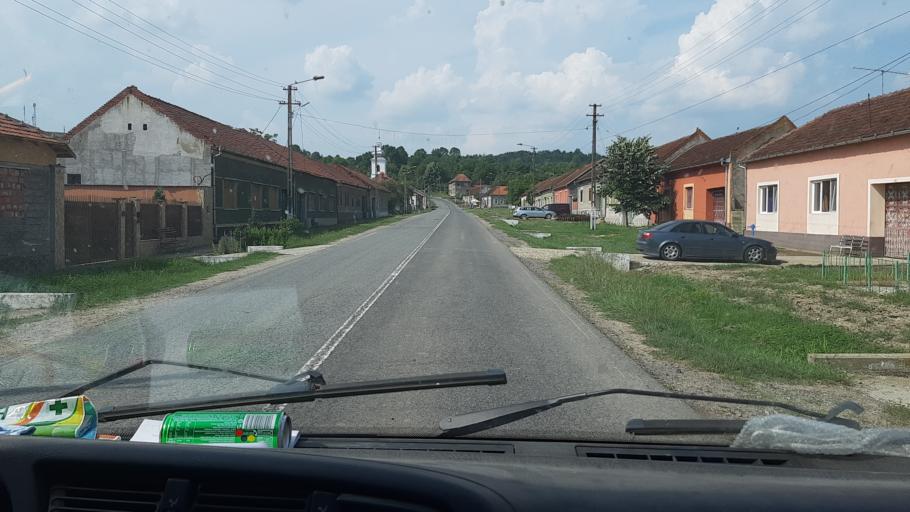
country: RO
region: Caras-Severin
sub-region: Comuna Farliug
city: Farliug
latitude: 45.5090
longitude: 21.8759
